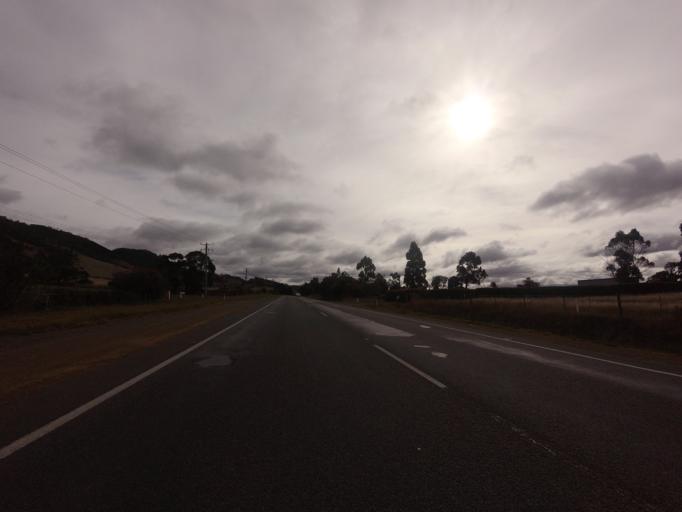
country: AU
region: Tasmania
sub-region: Brighton
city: Bridgewater
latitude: -42.6461
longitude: 147.2342
